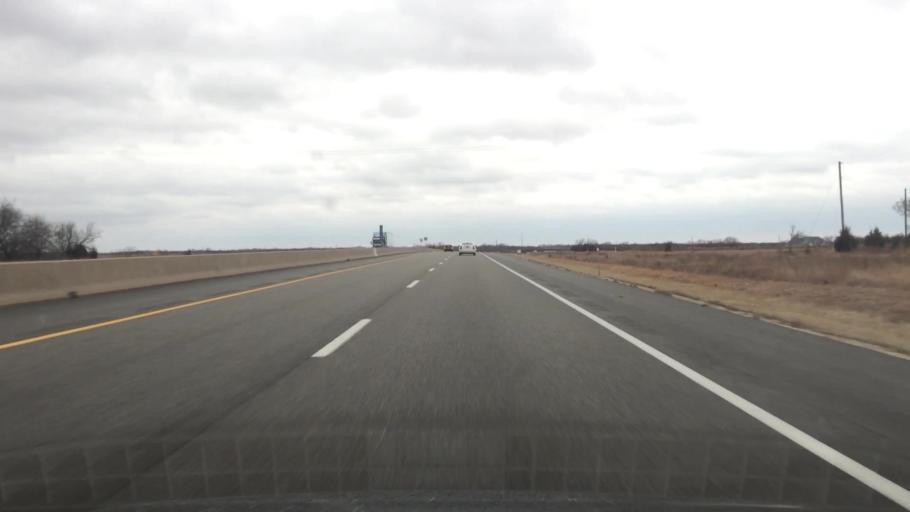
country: US
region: Kansas
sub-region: Butler County
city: Andover
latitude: 37.7379
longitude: -97.0659
